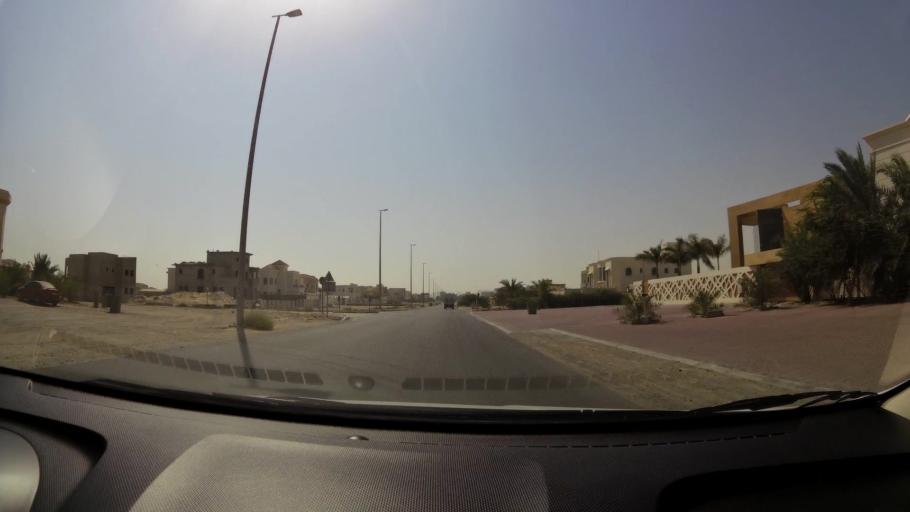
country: AE
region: Ajman
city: Ajman
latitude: 25.4104
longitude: 55.5357
